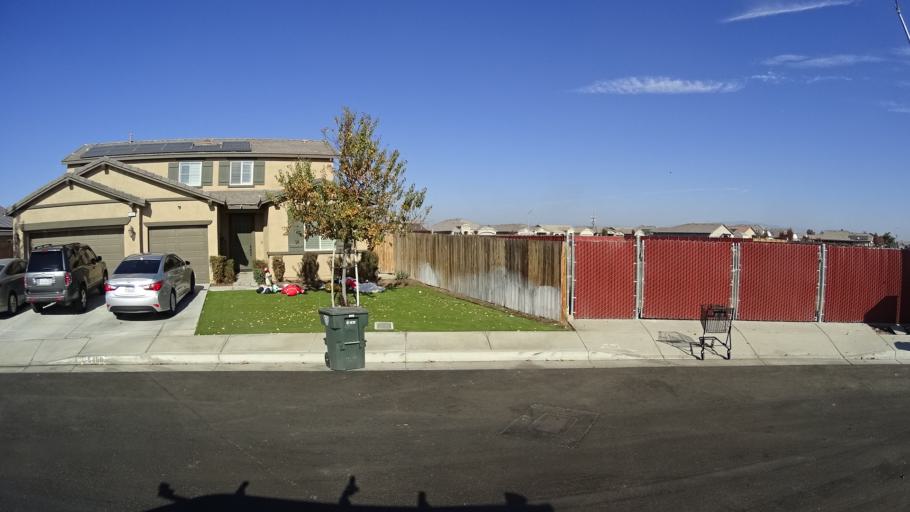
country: US
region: California
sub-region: Kern County
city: Greenfield
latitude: 35.2909
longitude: -119.0628
